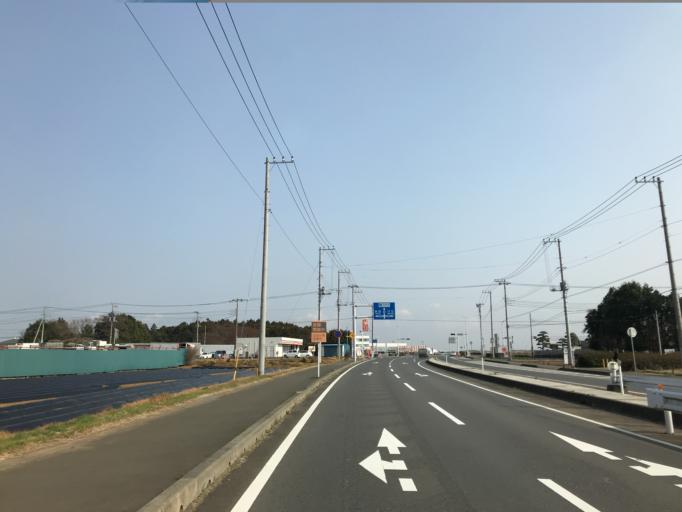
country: JP
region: Ibaraki
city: Okunoya
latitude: 36.1819
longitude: 140.4013
